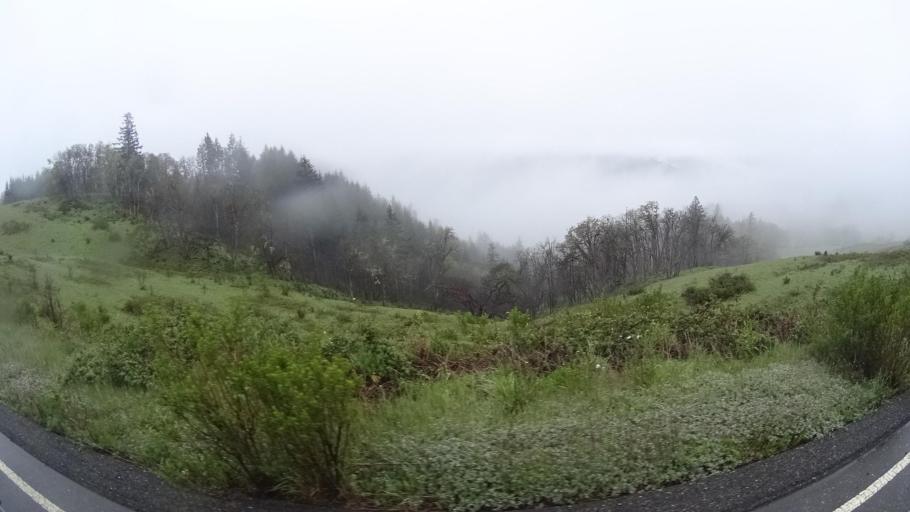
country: US
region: California
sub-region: Humboldt County
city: Westhaven-Moonstone
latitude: 41.1852
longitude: -123.9263
